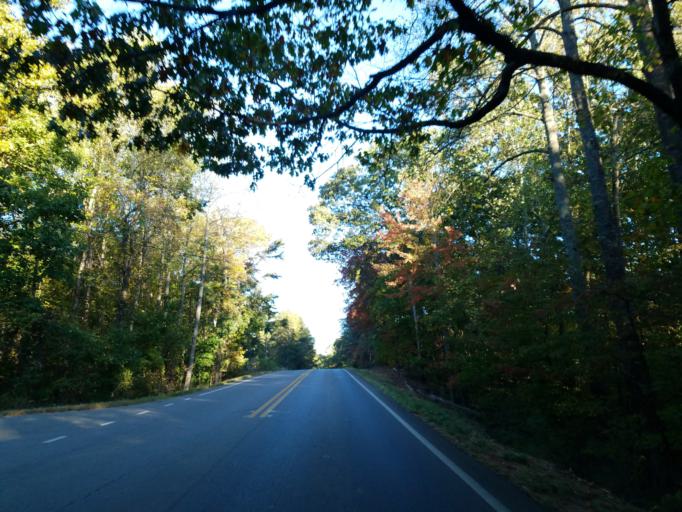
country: US
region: Georgia
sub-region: Dawson County
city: Dawsonville
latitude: 34.4219
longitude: -84.1988
